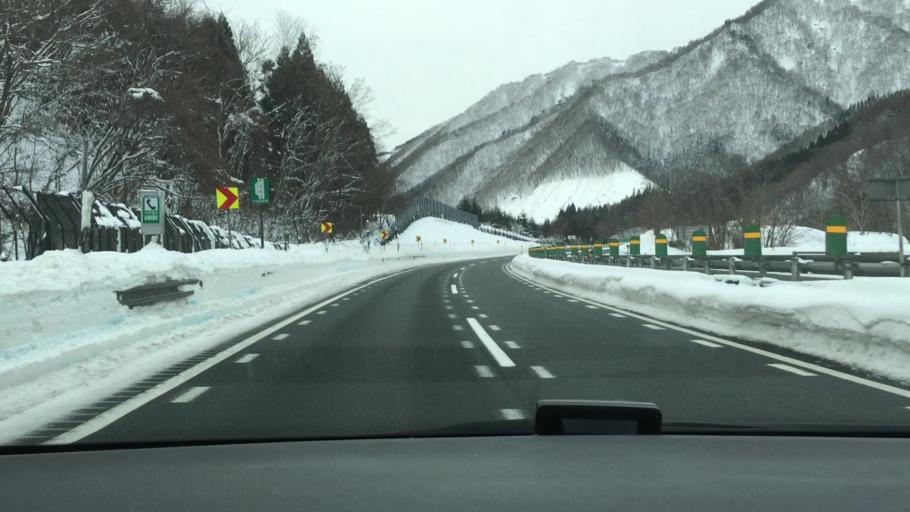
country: JP
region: Akita
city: Hanawa
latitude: 40.1316
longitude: 140.9246
